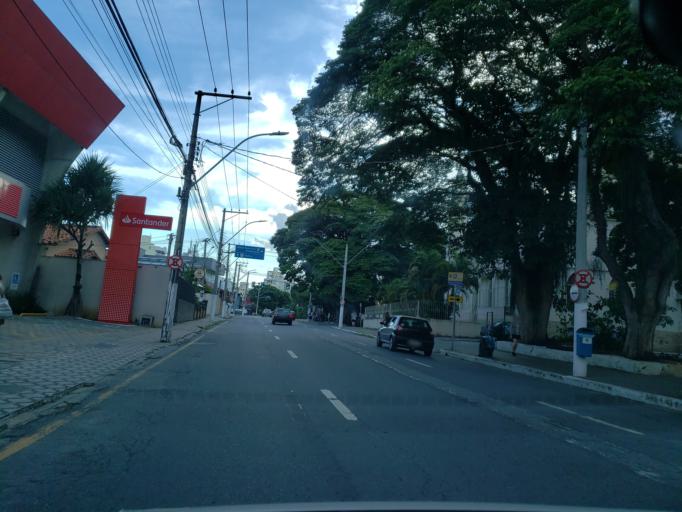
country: BR
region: Sao Paulo
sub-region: Taubate
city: Taubate
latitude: -23.0320
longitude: -45.5602
